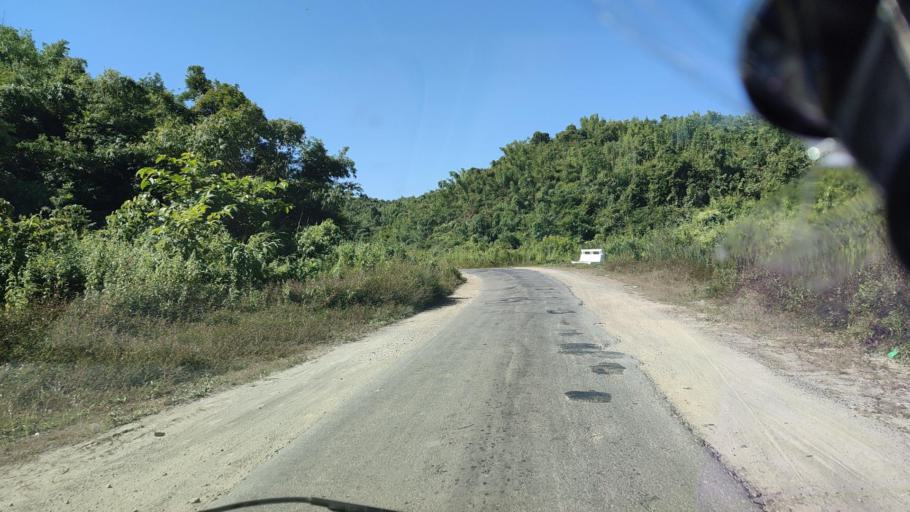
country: MM
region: Rakhine
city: Sittwe
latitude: 19.9796
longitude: 93.6241
